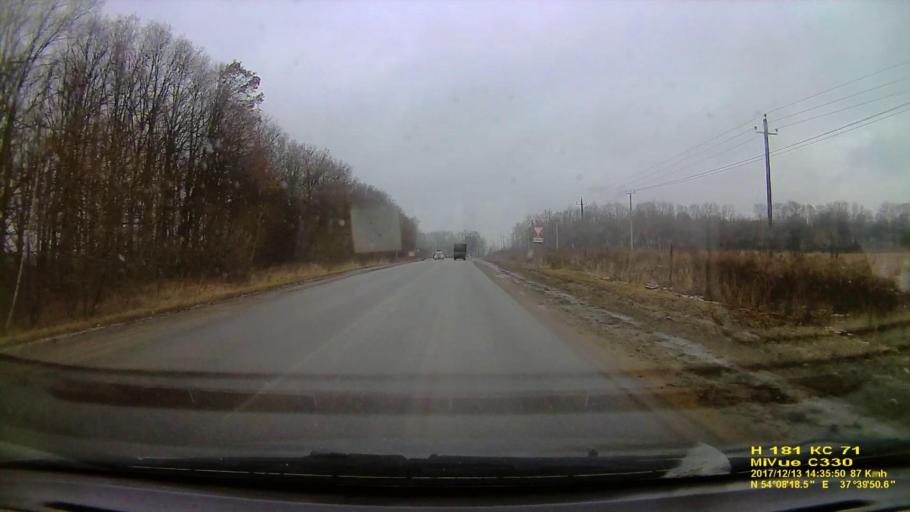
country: RU
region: Tula
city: Skuratovskiy
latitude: 54.1387
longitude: 37.6640
